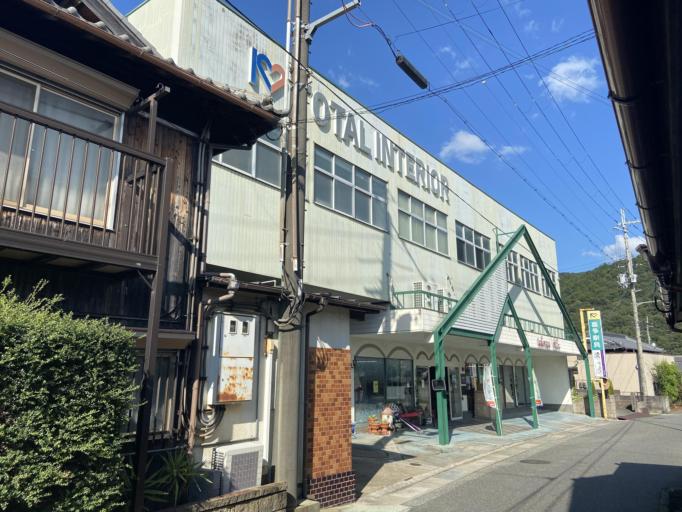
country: JP
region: Hyogo
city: Nishiwaki
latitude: 34.9737
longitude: 134.9720
